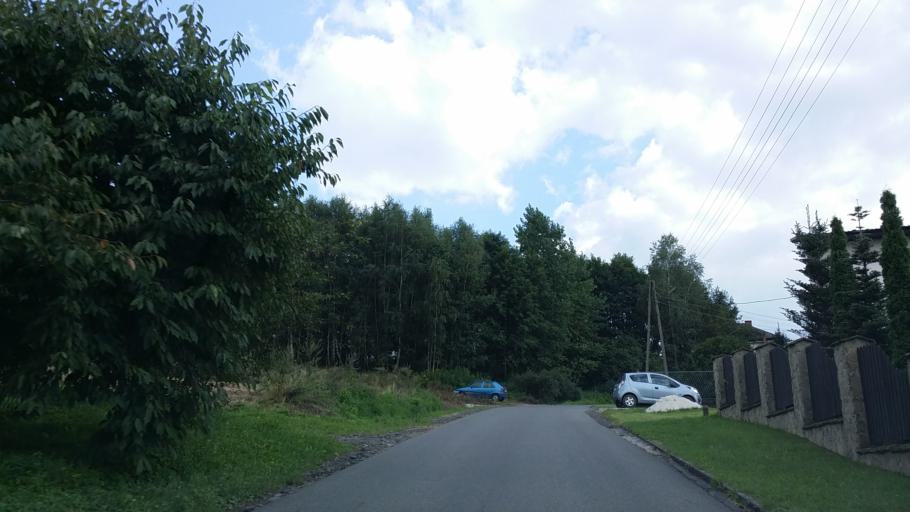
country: PL
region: Lesser Poland Voivodeship
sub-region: Powiat wadowicki
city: Spytkowice
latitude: 49.9899
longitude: 19.4764
